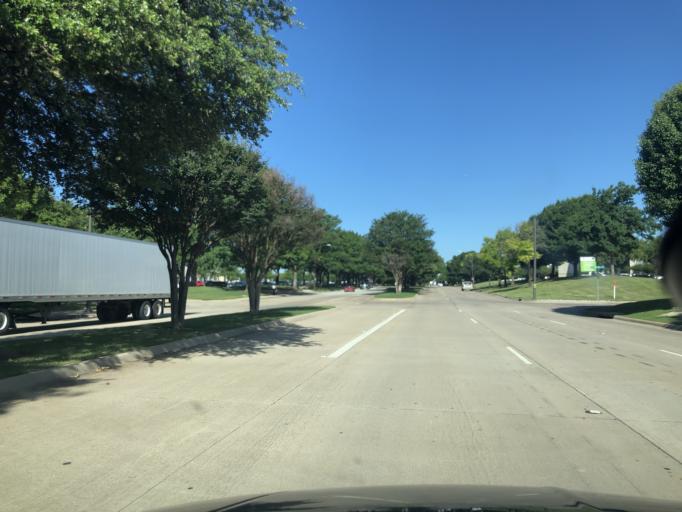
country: US
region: Texas
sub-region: Tarrant County
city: Euless
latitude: 32.8221
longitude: -97.0436
